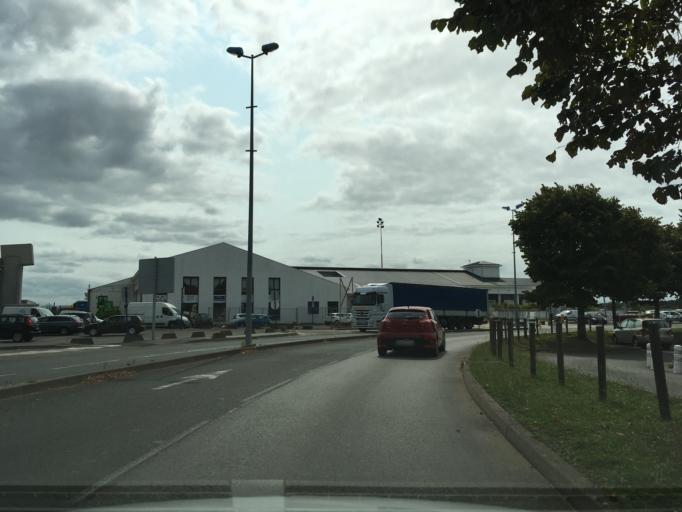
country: FR
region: Aquitaine
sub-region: Departement des Pyrenees-Atlantiques
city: Anglet
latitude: 43.4718
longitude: -1.5333
